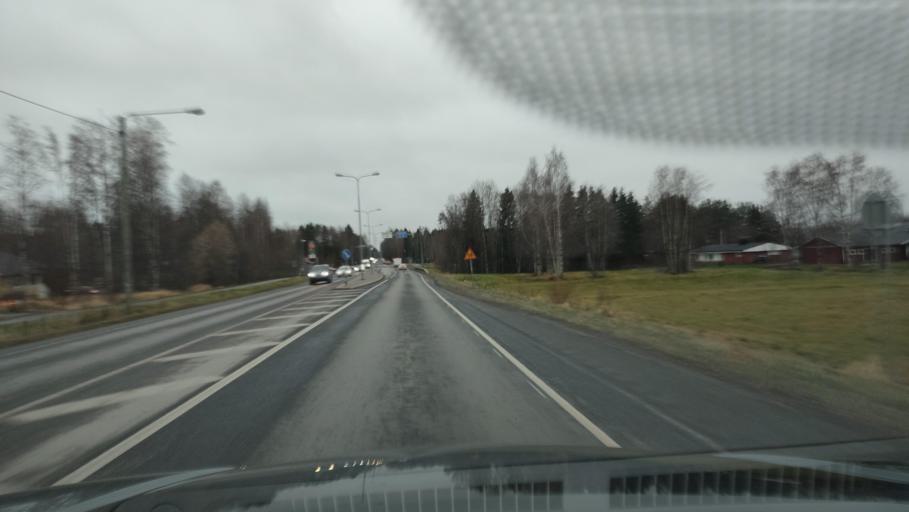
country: FI
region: Southern Ostrobothnia
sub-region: Seinaejoki
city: Ilmajoki
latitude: 62.7720
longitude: 22.6826
